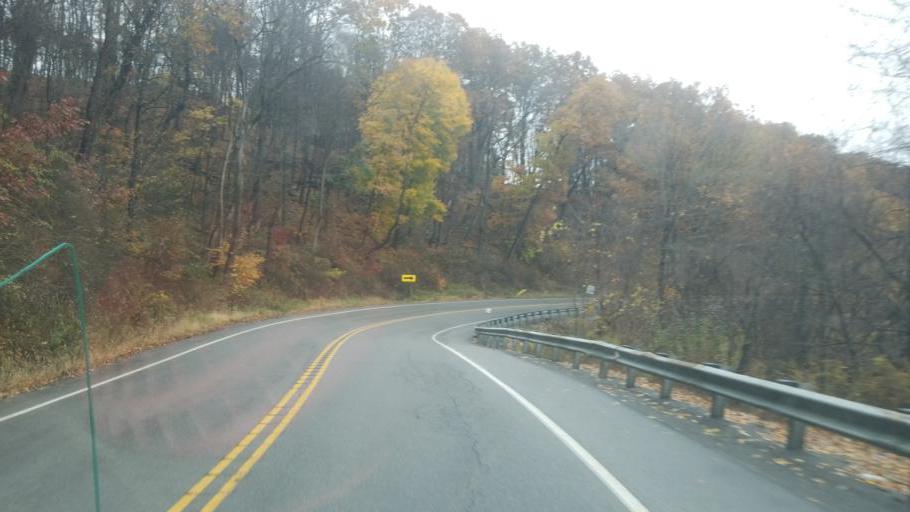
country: US
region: Pennsylvania
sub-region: Clearfield County
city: Clearfield
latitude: 41.0424
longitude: -78.3870
